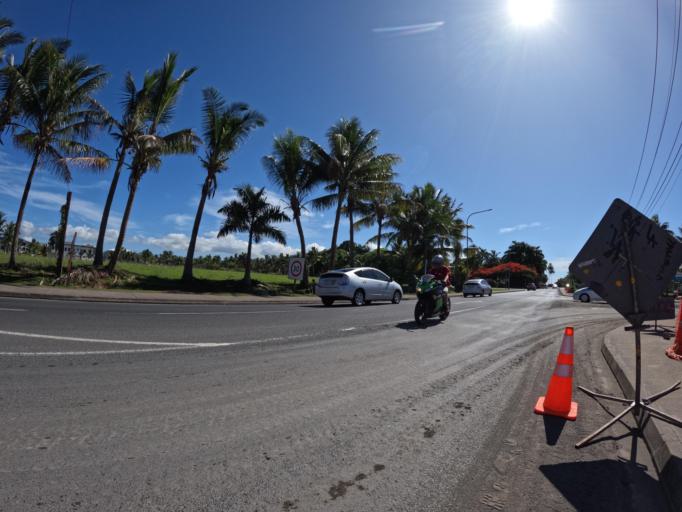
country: FJ
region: Central
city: Suva
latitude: -18.1488
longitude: 178.4517
